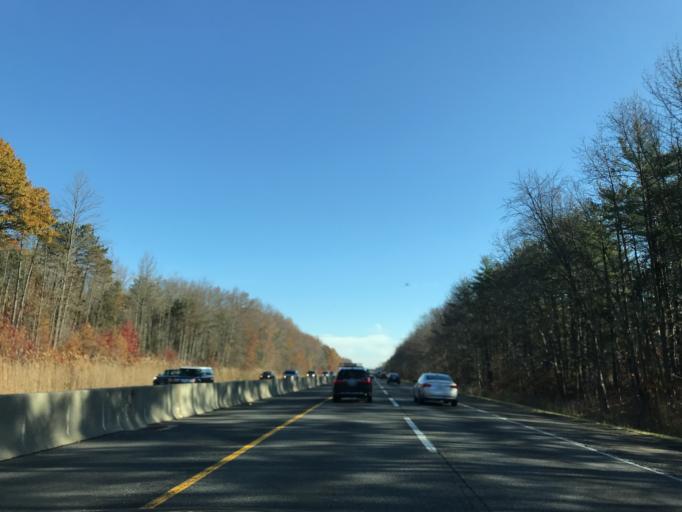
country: US
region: New Jersey
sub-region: Salem County
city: Carneys Point
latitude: 39.6917
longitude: -75.4130
